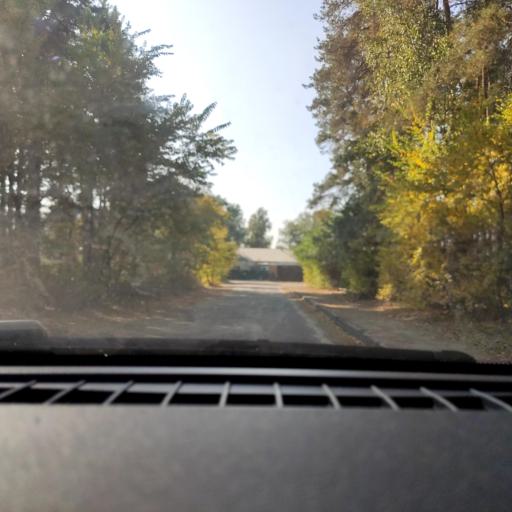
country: RU
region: Voronezj
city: Maslovka
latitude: 51.5472
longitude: 39.2213
